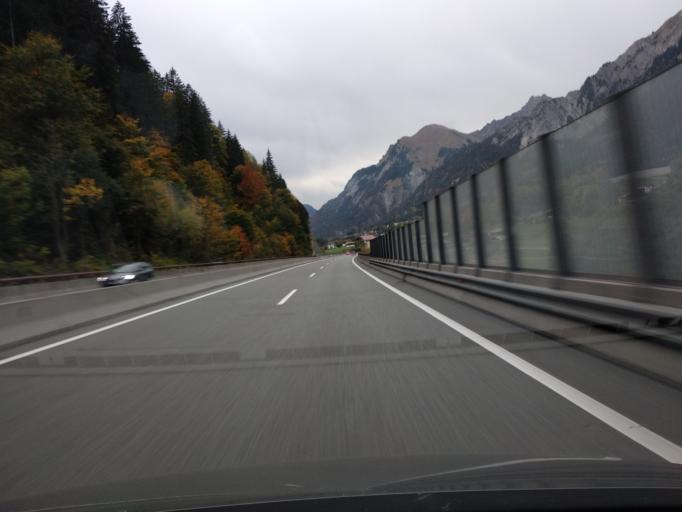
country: AT
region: Vorarlberg
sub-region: Politischer Bezirk Bludenz
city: Klosterle
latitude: 47.1301
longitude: 10.0726
